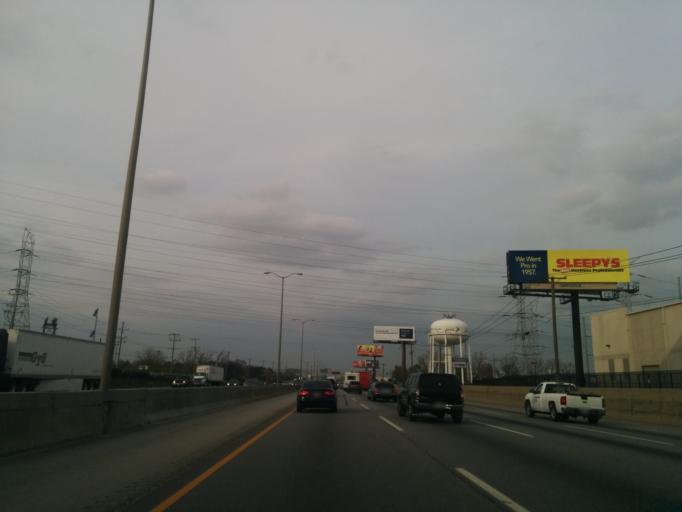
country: US
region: Illinois
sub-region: Cook County
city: Northlake
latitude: 41.9230
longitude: -87.9196
